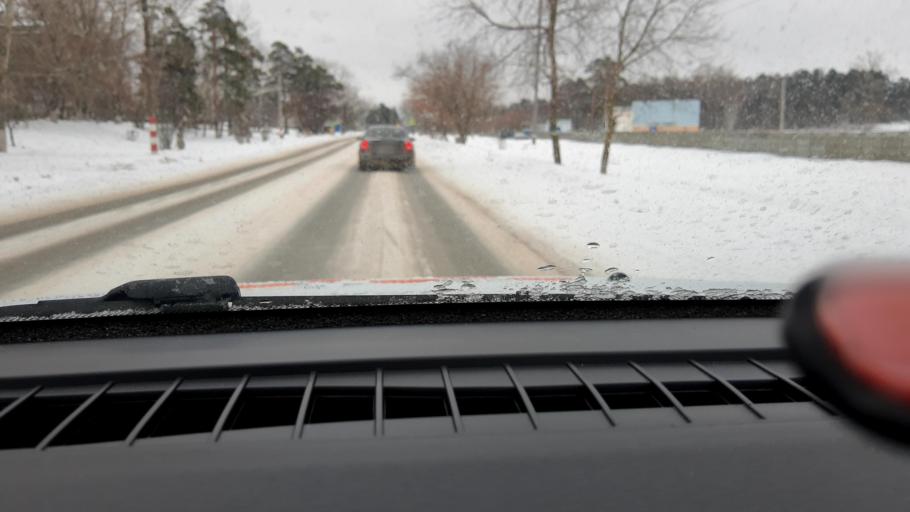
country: RU
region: Nizjnij Novgorod
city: Bor
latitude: 56.3316
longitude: 44.1147
